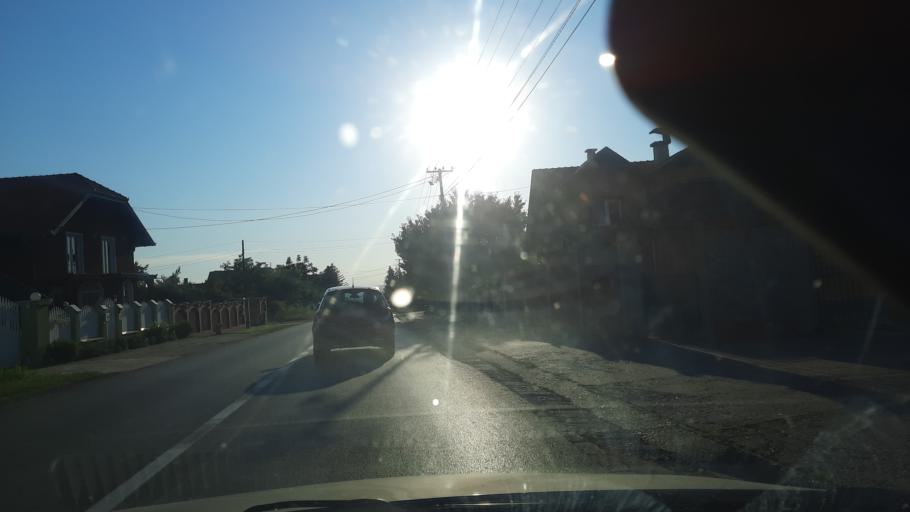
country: RS
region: Central Serbia
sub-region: Branicevski Okrug
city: Malo Crnice
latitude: 44.5730
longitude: 21.3623
